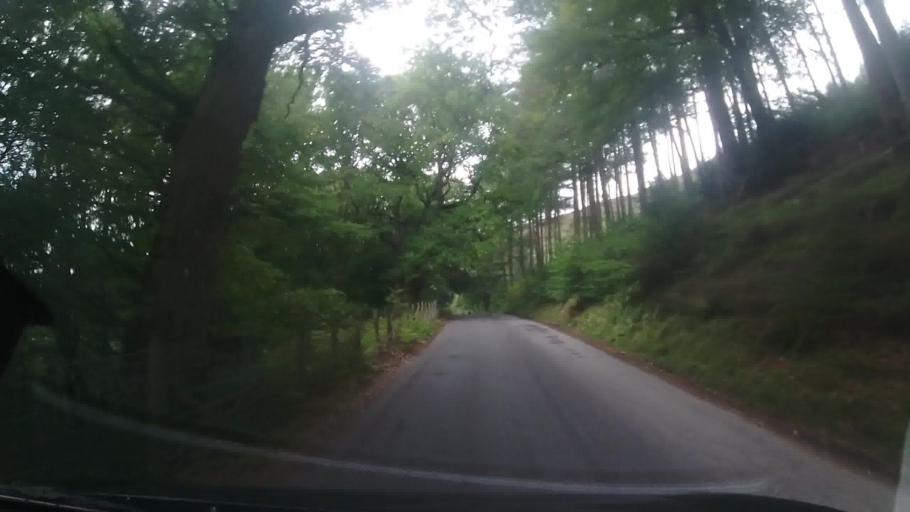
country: GB
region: Wales
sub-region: Sir Powys
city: Rhayader
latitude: 52.2675
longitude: -3.5938
